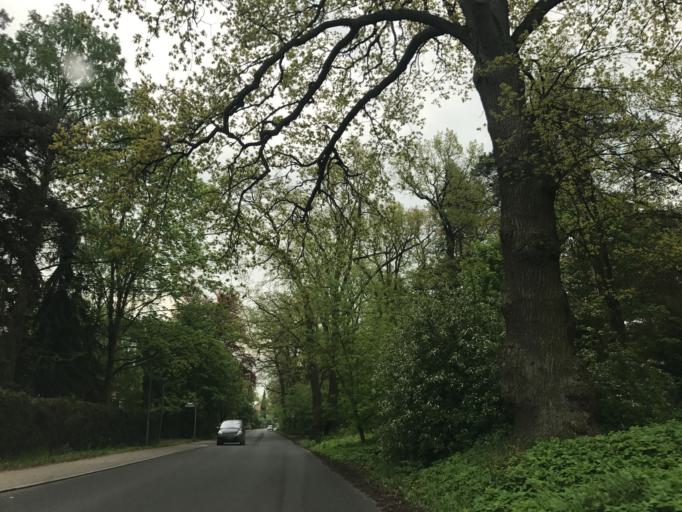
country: DE
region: Berlin
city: Falkenhagener Feld
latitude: 52.5577
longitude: 13.1835
